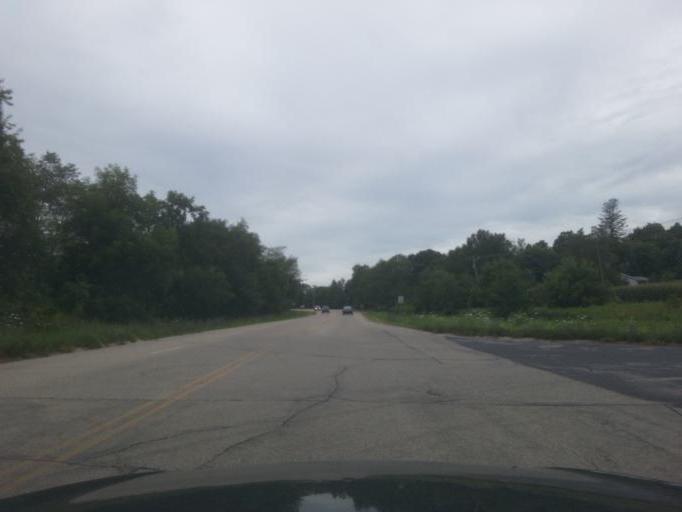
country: US
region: Wisconsin
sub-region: Dane County
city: Monona
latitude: 43.0750
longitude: -89.2697
